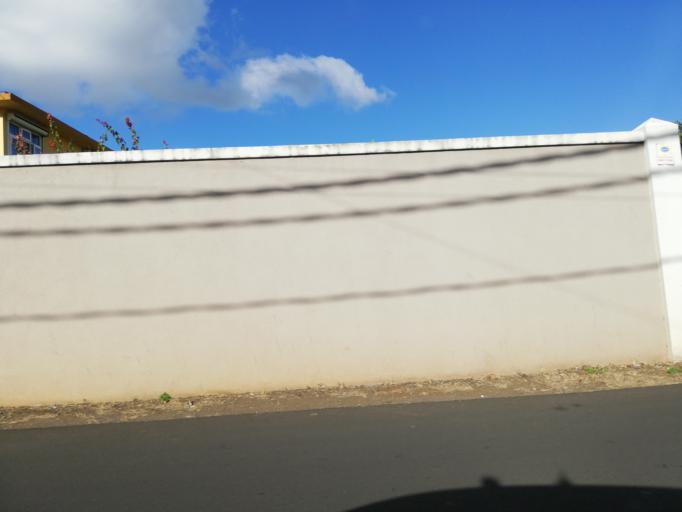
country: MU
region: Moka
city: Moka
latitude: -20.2221
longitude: 57.4755
